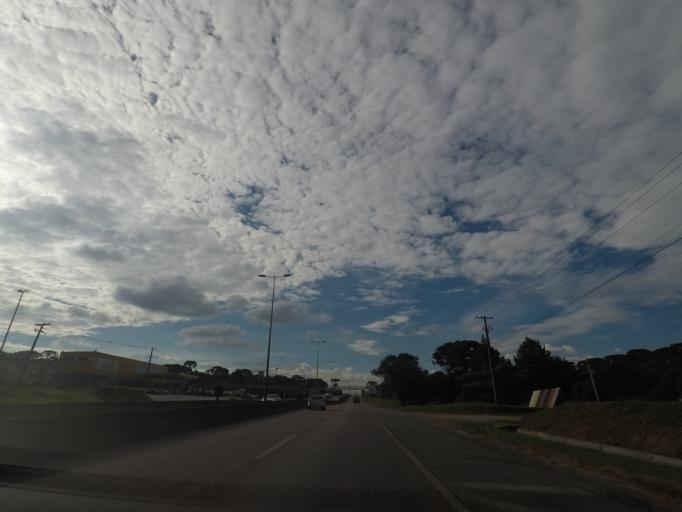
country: BR
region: Parana
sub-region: Araucaria
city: Araucaria
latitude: -25.6075
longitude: -49.3190
